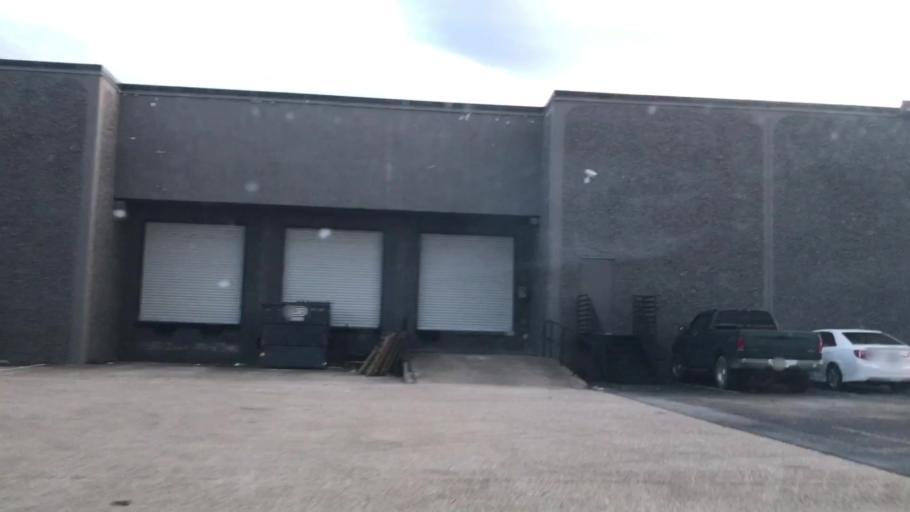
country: US
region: Texas
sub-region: Dallas County
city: Addison
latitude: 32.9329
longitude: -96.8311
